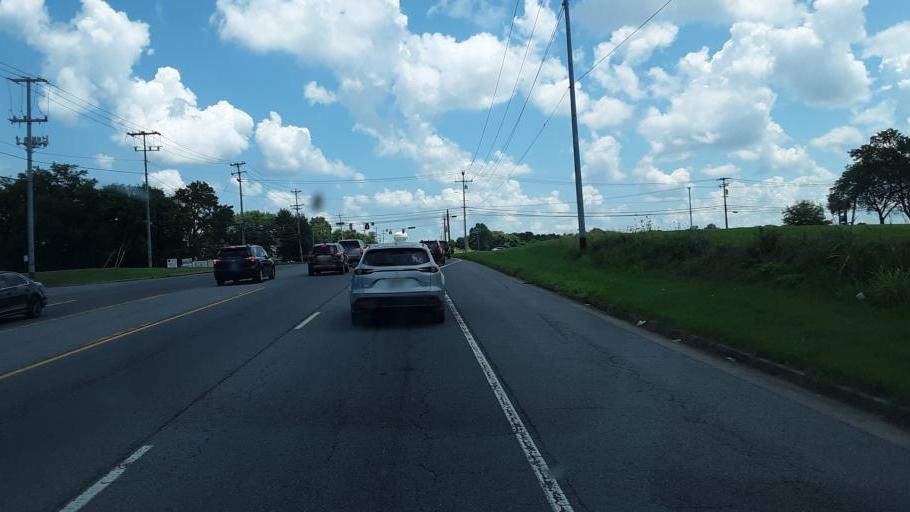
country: US
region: Kentucky
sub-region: Christian County
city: Oak Grove
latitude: 36.6268
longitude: -87.3608
